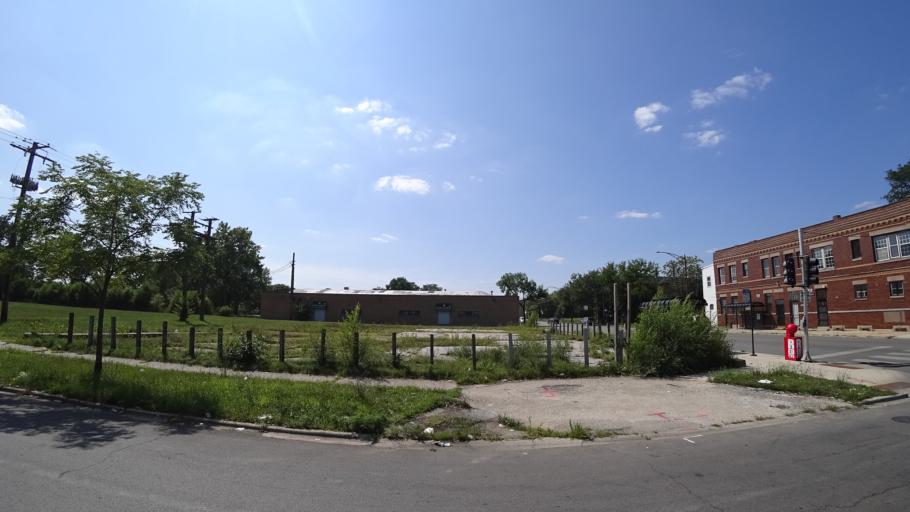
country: US
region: Illinois
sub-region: Cook County
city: Cicero
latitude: 41.8586
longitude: -87.7298
